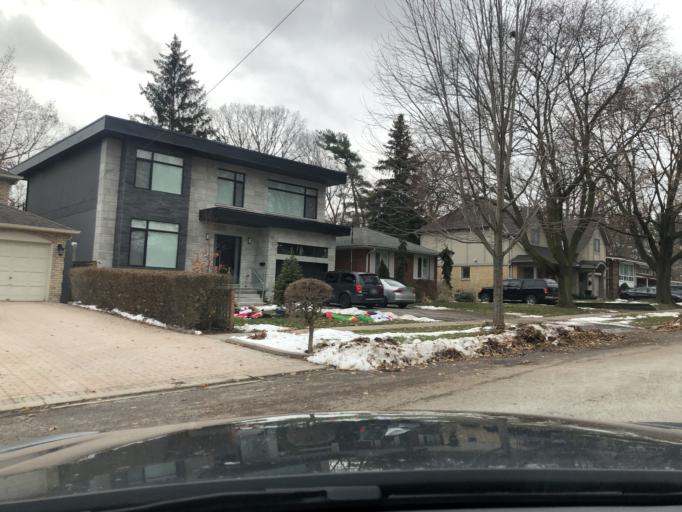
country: CA
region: Ontario
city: Etobicoke
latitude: 43.6913
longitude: -79.5197
